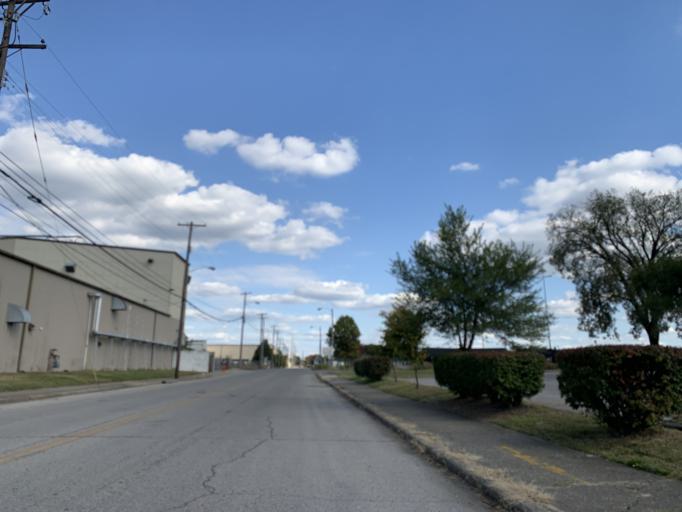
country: US
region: Kentucky
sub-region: Jefferson County
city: Louisville
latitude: 38.2413
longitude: -85.7773
